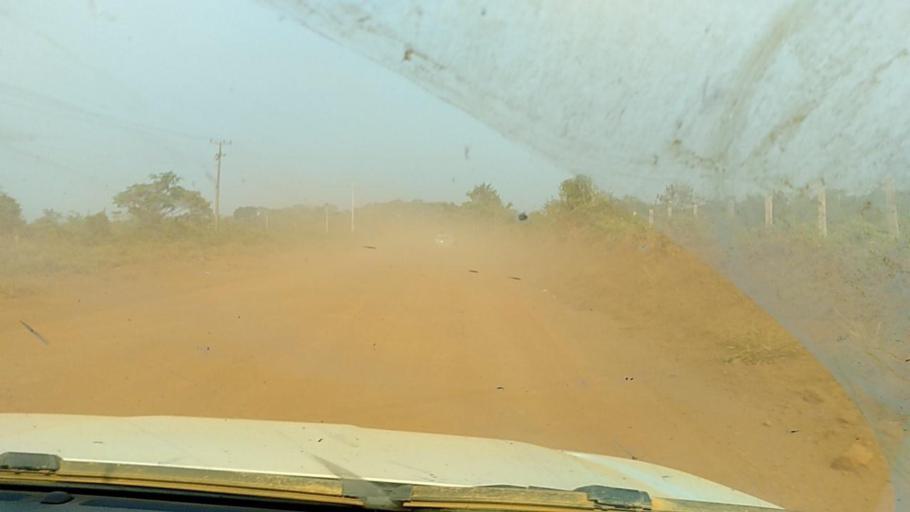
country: BR
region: Rondonia
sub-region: Porto Velho
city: Porto Velho
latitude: -8.7599
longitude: -63.9758
